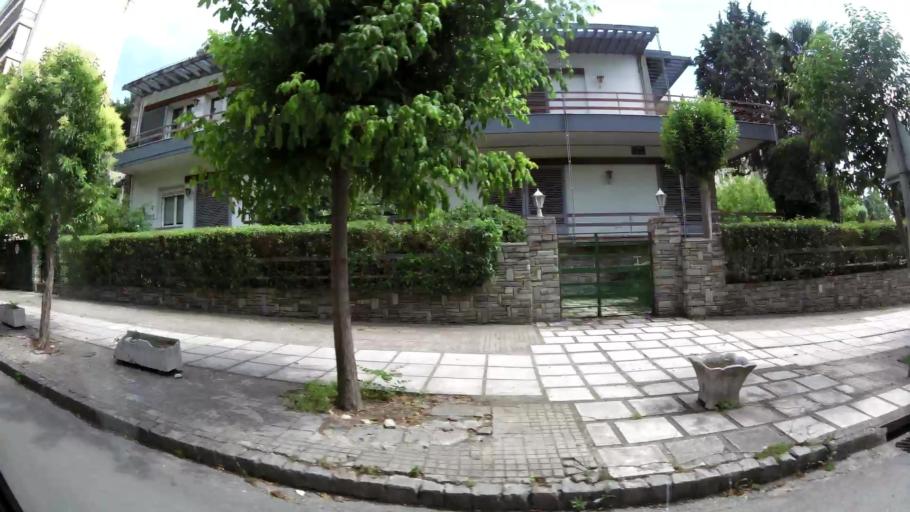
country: GR
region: Central Macedonia
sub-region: Nomos Thessalonikis
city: Kalamaria
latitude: 40.5932
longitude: 22.9525
